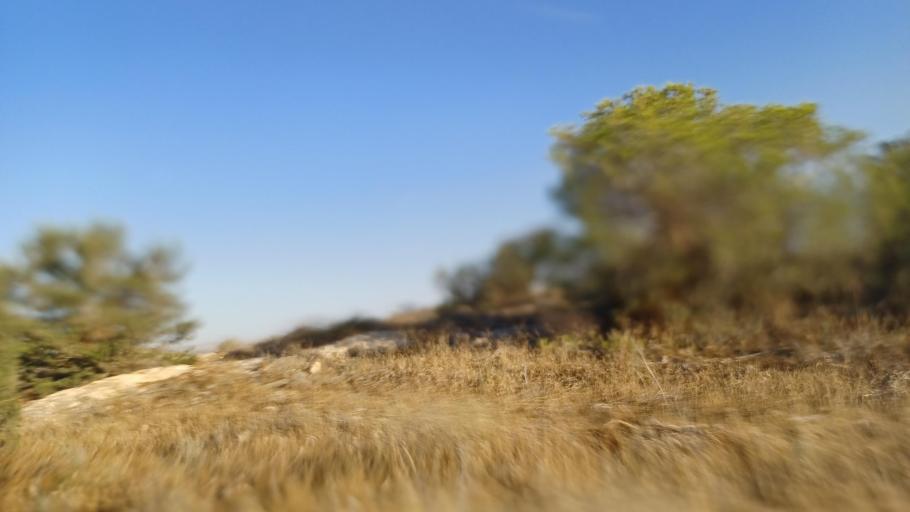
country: CY
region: Larnaka
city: Pyla
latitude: 34.9869
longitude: 33.7061
